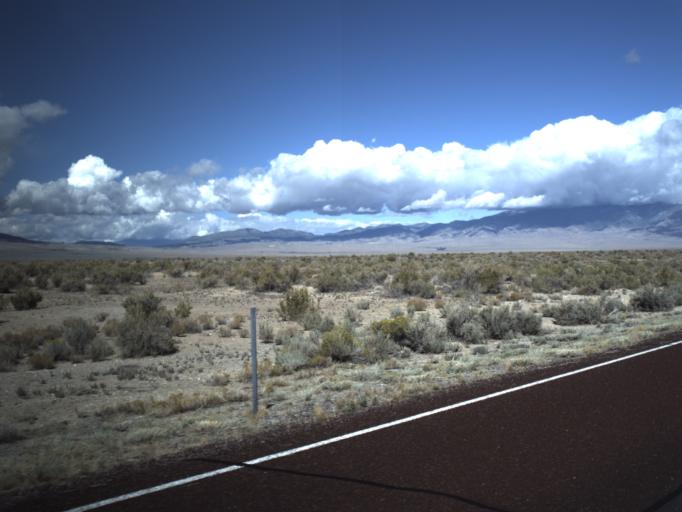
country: US
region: Nevada
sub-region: White Pine County
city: McGill
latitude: 38.9512
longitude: -114.0332
